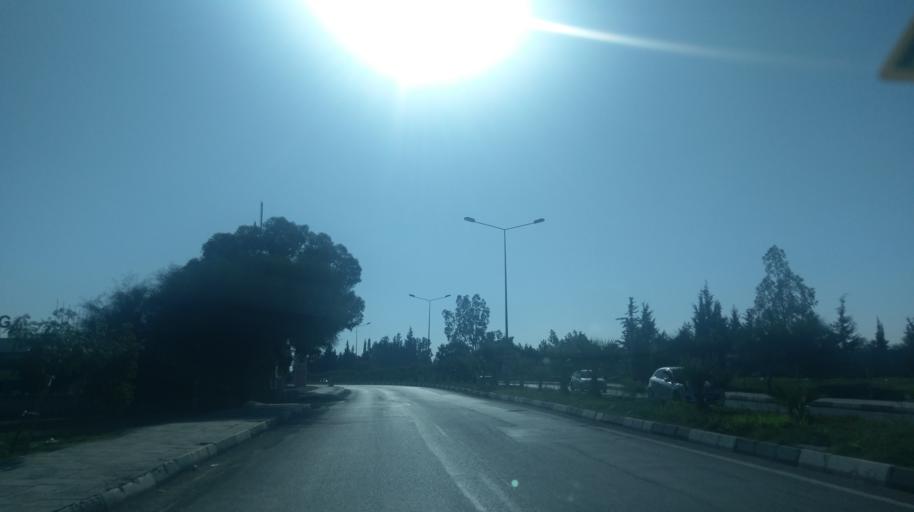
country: CY
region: Lefkosia
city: Nicosia
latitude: 35.2214
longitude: 33.3286
